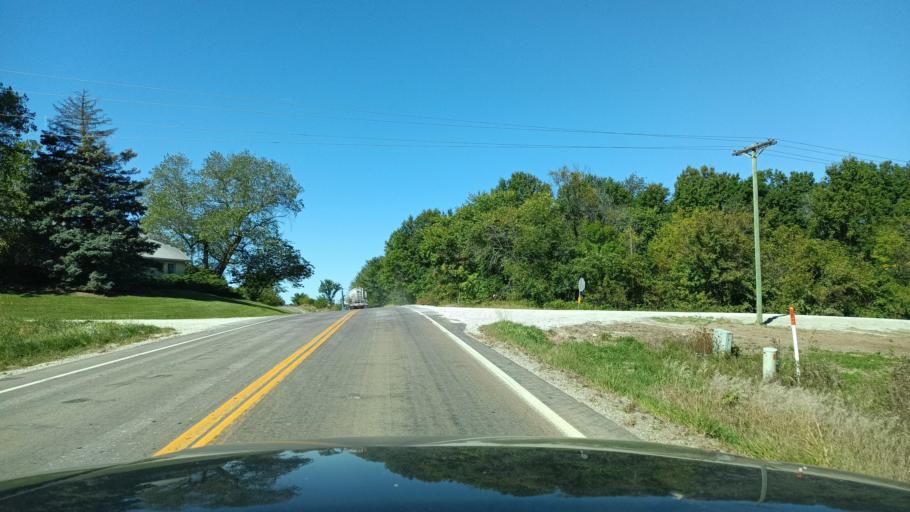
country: US
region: Missouri
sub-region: Scotland County
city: Memphis
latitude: 40.4554
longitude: -92.0576
